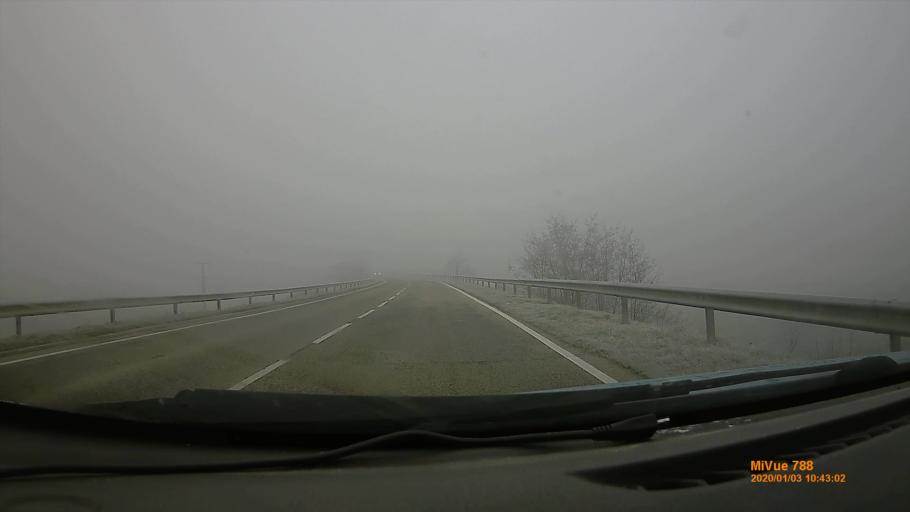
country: HU
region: Tolna
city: Bataszek
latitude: 46.2072
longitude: 18.7077
